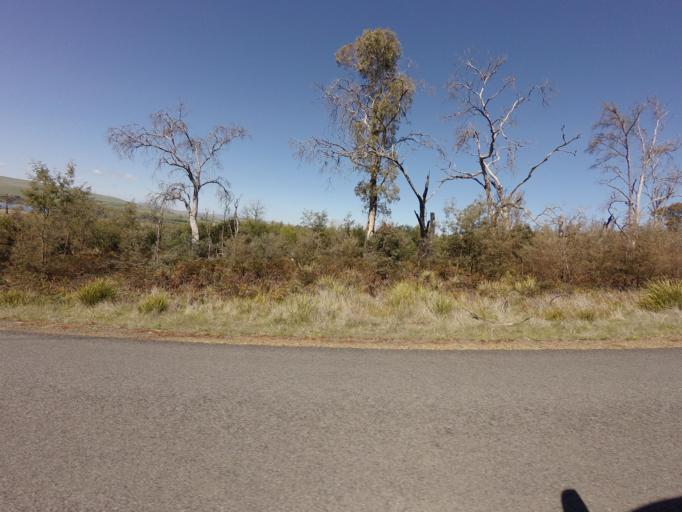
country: AU
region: Tasmania
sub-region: Derwent Valley
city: New Norfolk
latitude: -42.5394
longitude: 146.7210
